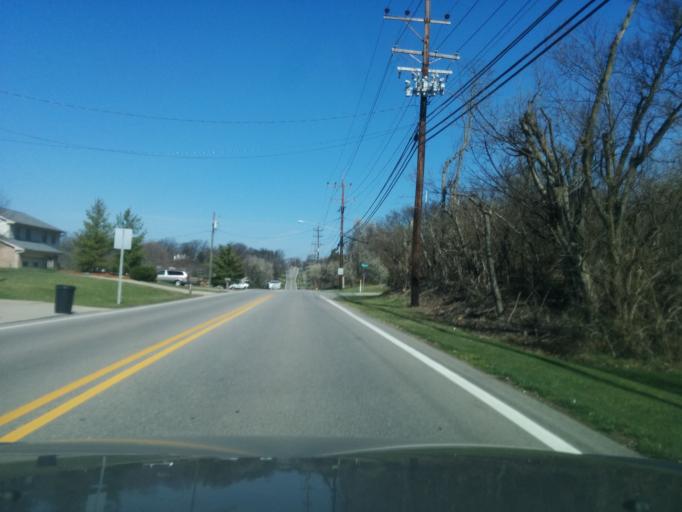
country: US
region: Ohio
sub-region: Hamilton County
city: Dent
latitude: 39.1891
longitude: -84.6278
